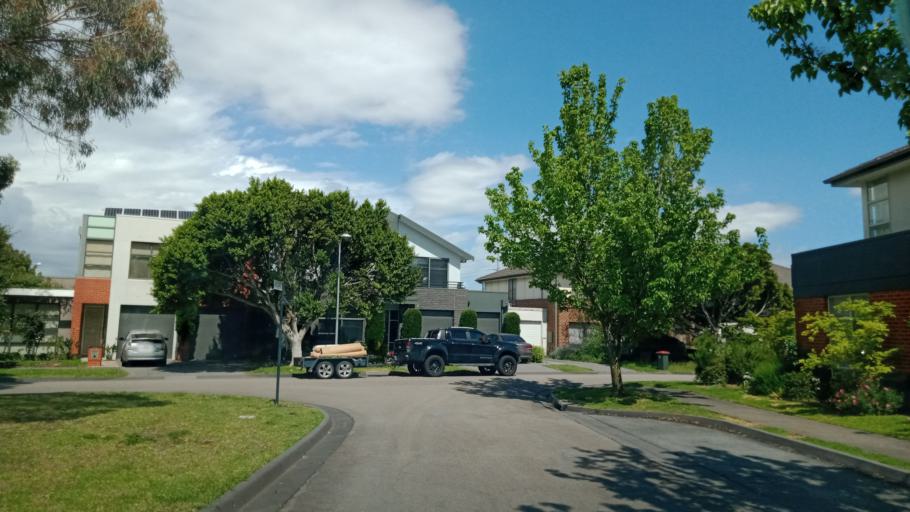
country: AU
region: Victoria
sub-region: Monash
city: Mulgrave
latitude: -37.9266
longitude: 145.1855
